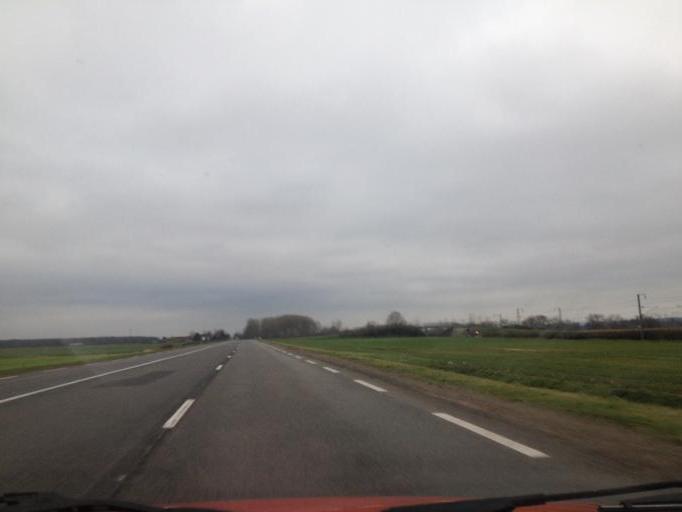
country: FR
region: Auvergne
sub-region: Departement de l'Allier
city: Bessay-sur-Allier
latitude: 46.4177
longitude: 3.3541
